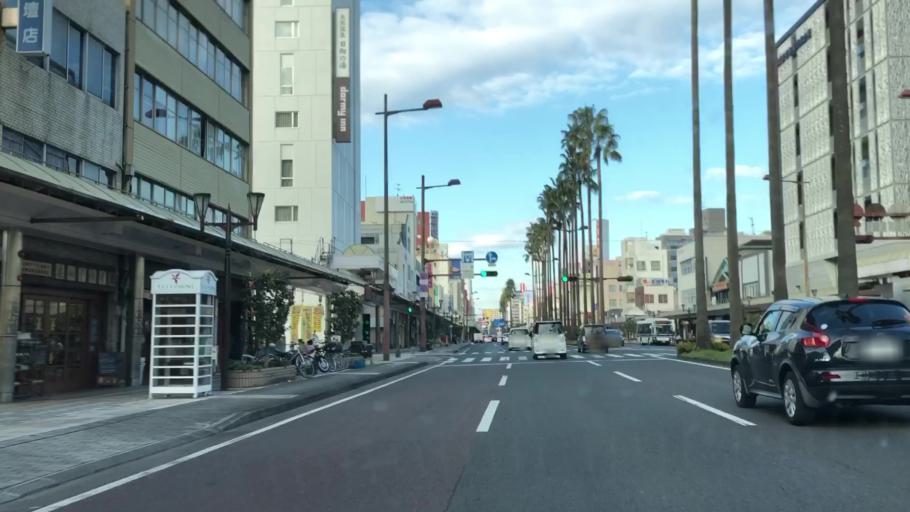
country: JP
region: Miyazaki
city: Miyazaki-shi
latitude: 31.9111
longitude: 131.4222
